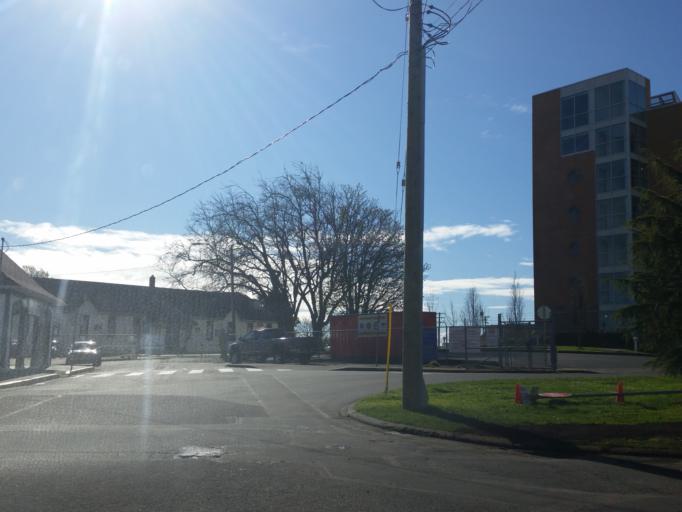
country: CA
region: British Columbia
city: Victoria
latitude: 48.4262
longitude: -123.3983
